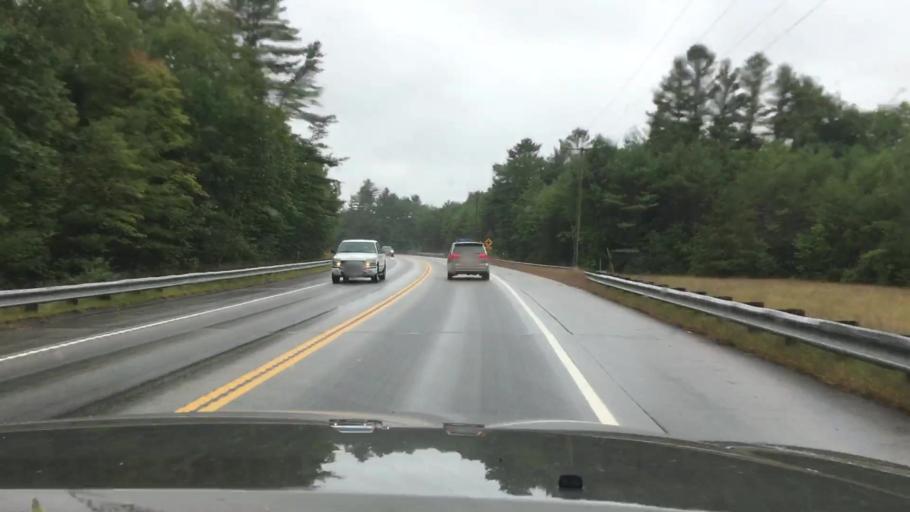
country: US
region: New Hampshire
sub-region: Cheshire County
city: Keene
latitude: 42.9304
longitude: -72.3259
